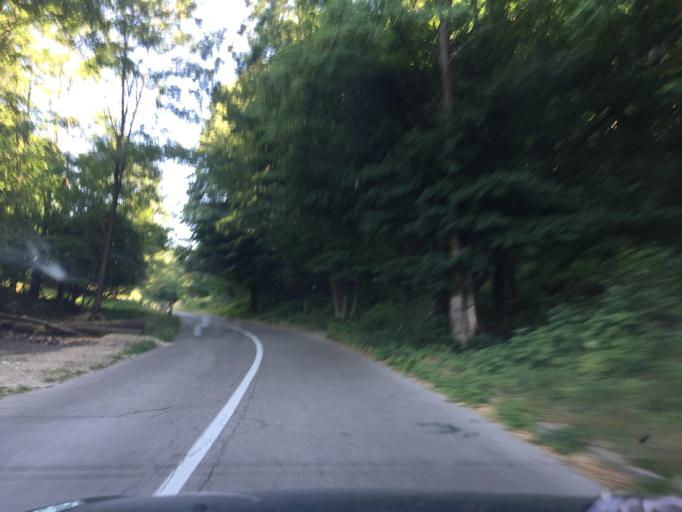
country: HR
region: Primorsko-Goranska
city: Klana
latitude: 45.4354
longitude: 14.3885
